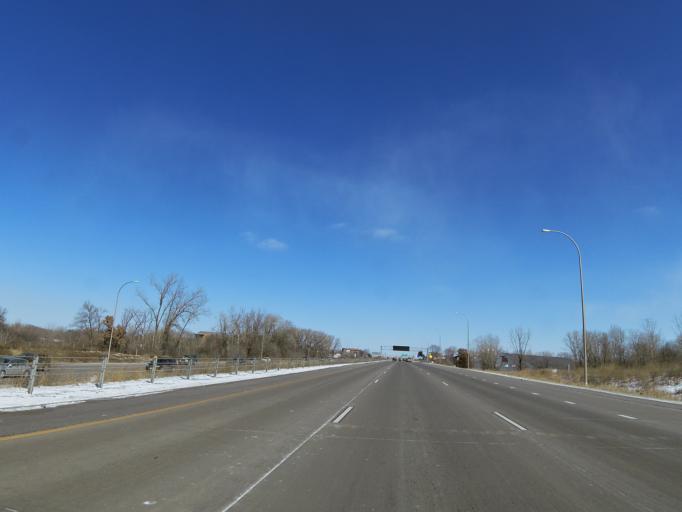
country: US
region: Minnesota
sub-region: Washington County
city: Woodbury
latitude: 44.9164
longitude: -92.9788
